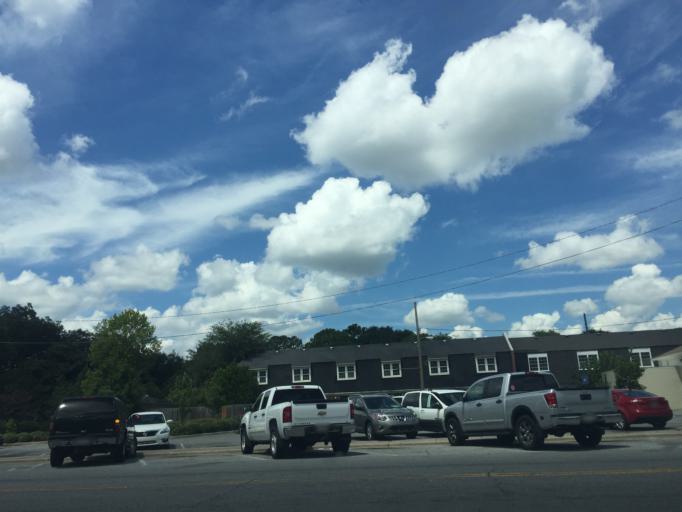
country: US
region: Georgia
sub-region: Chatham County
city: Savannah
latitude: 32.0349
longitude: -81.1034
